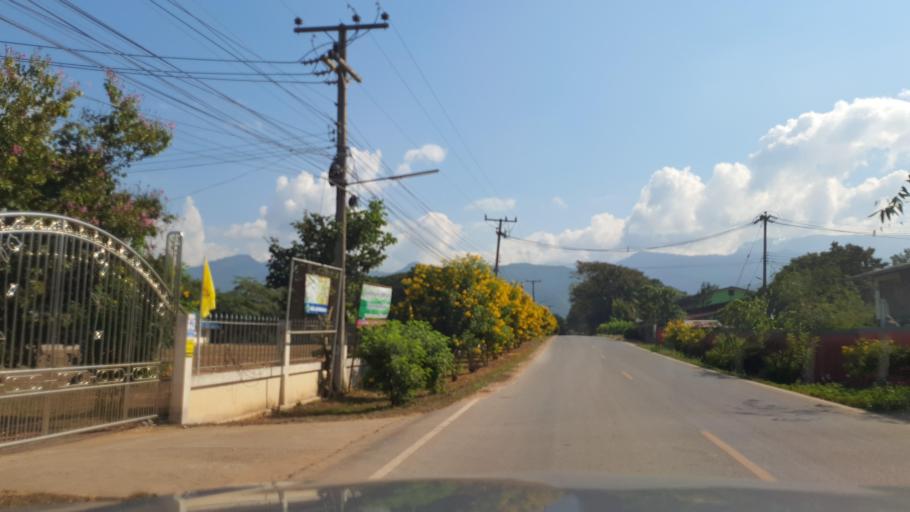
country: TH
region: Nan
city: Pua
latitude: 19.1409
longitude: 100.9293
